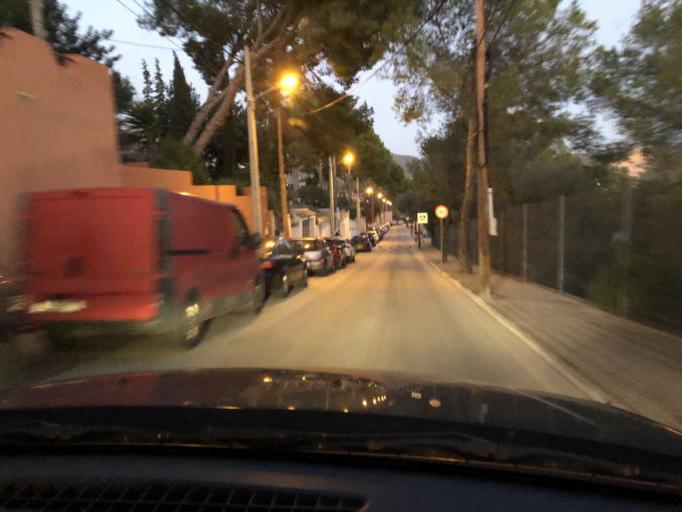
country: ES
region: Balearic Islands
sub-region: Illes Balears
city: Santa Ponsa
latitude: 39.5223
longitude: 2.4869
